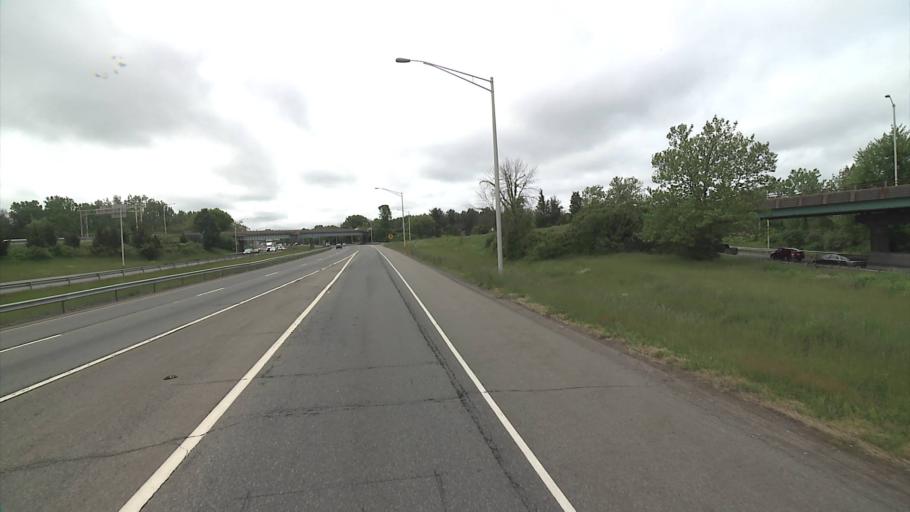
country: US
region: Connecticut
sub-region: New Haven County
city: Meriden
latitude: 41.5225
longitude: -72.7715
